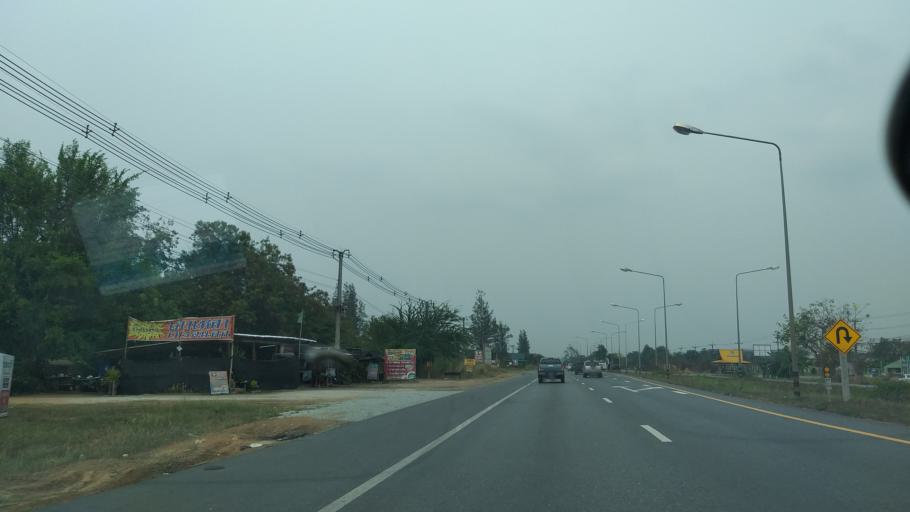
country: TH
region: Chon Buri
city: Ko Chan
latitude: 13.2996
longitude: 101.2615
